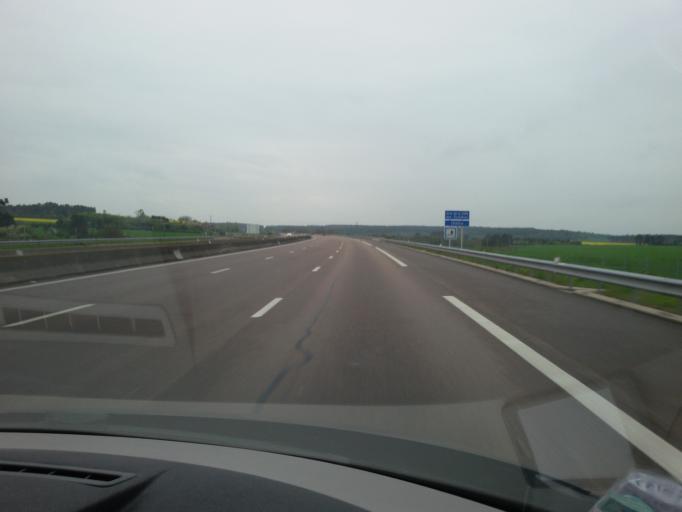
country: FR
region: Bourgogne
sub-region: Departement de la Cote-d'Or
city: Selongey
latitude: 47.5738
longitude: 5.2087
